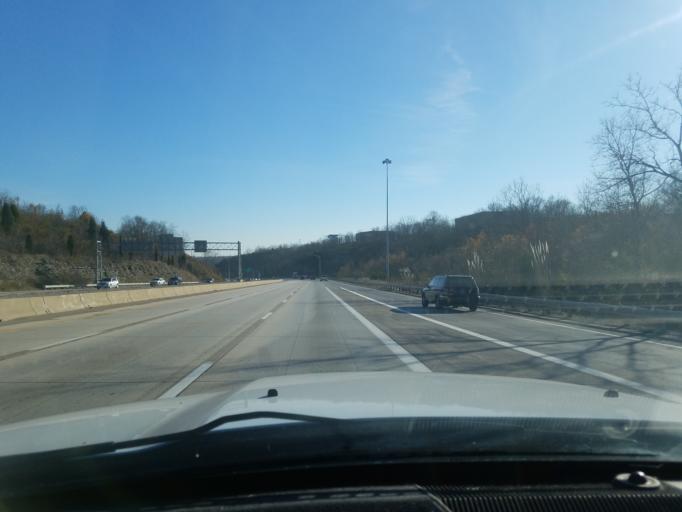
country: US
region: Kentucky
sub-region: Kenton County
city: Lakeside Park
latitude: 39.0256
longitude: -84.5637
